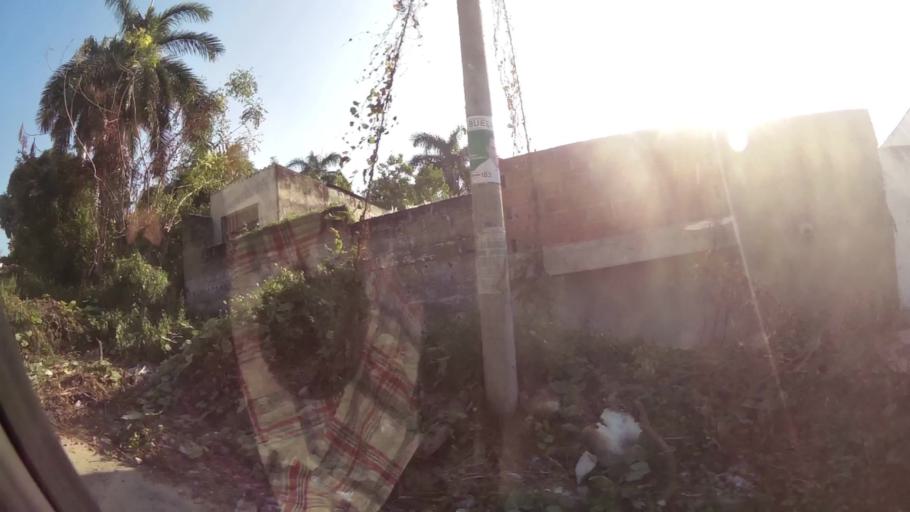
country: CO
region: Bolivar
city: Cartagena
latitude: 10.4031
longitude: -75.4806
